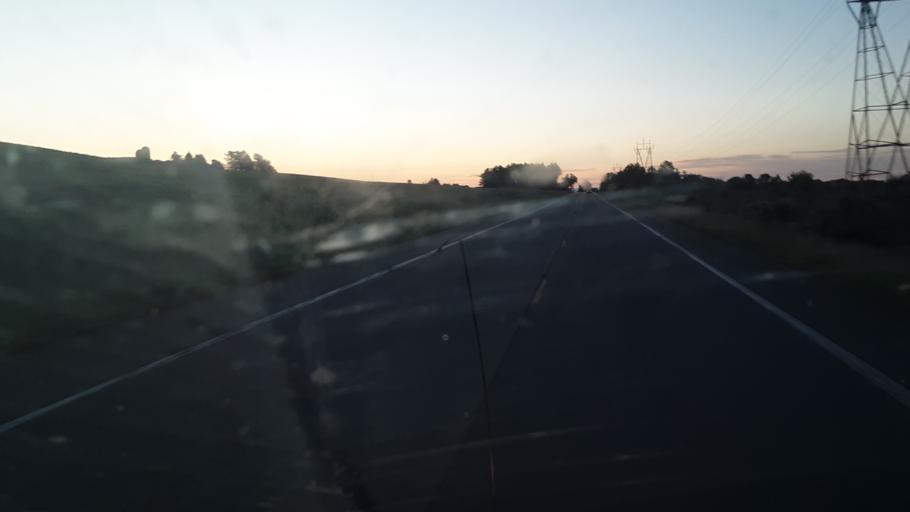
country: US
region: New York
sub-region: Montgomery County
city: Hagaman
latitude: 42.9737
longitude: -74.0452
